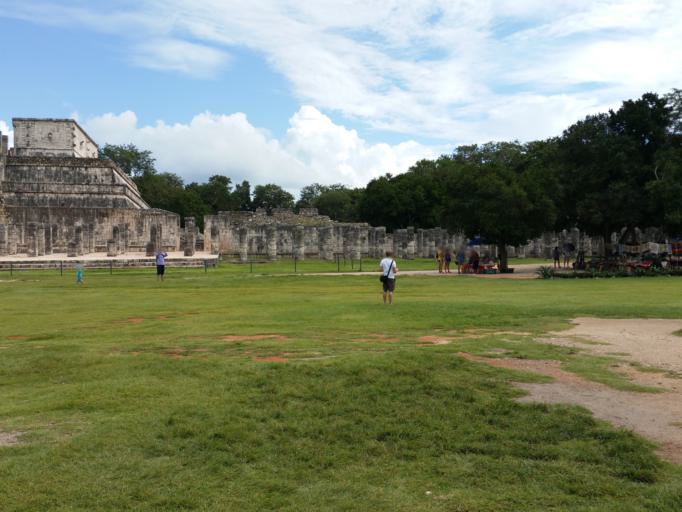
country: MX
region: Yucatan
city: Chichen-Itza
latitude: 20.6831
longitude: -88.5681
